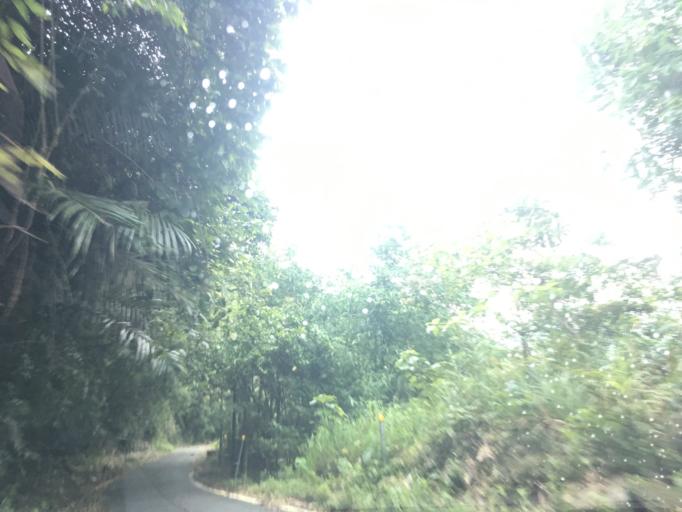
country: TW
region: Taiwan
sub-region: Yunlin
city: Douliu
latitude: 23.5687
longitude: 120.6358
